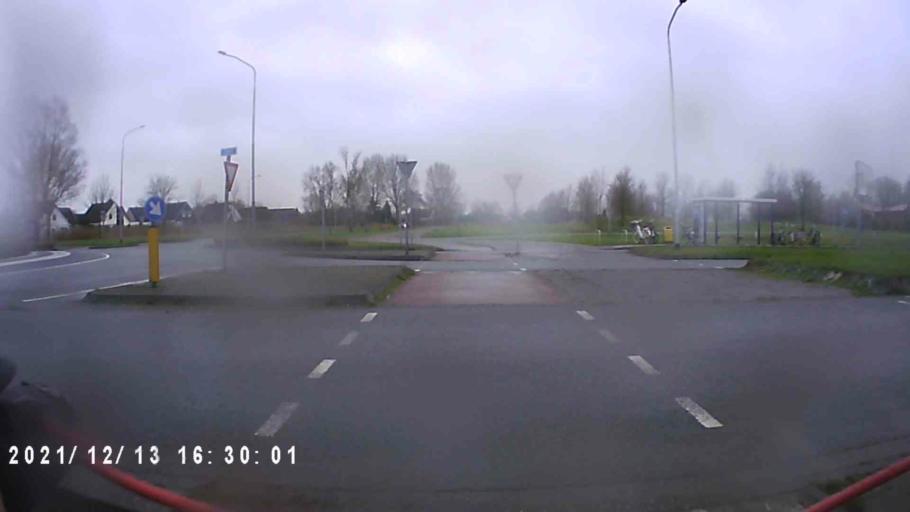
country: NL
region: Groningen
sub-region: Gemeente Appingedam
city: Appingedam
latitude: 53.3224
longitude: 6.8884
